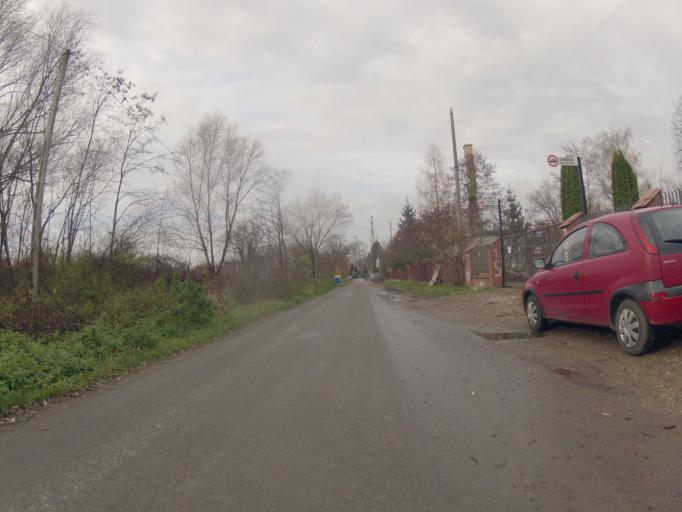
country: PL
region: Lesser Poland Voivodeship
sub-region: Powiat krakowski
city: Rzaska
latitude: 50.0810
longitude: 19.8509
